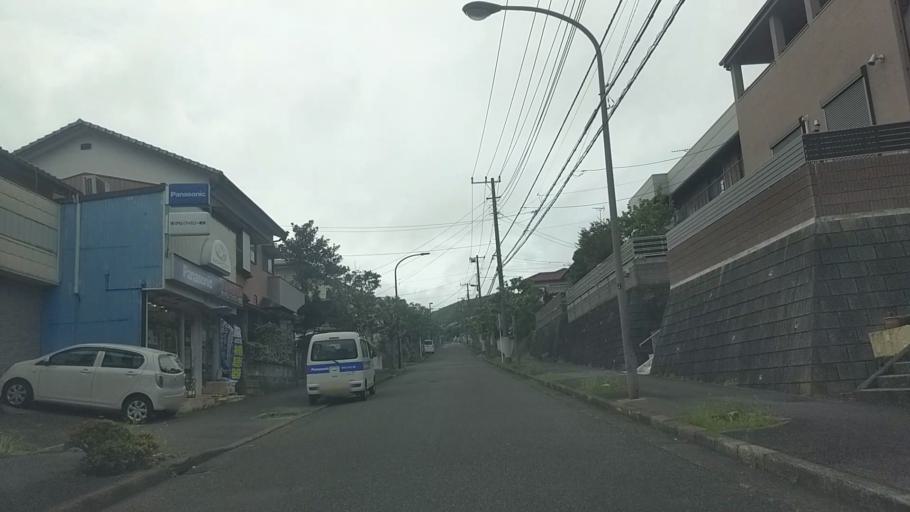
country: JP
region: Kanagawa
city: Yokosuka
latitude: 35.2535
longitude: 139.7363
